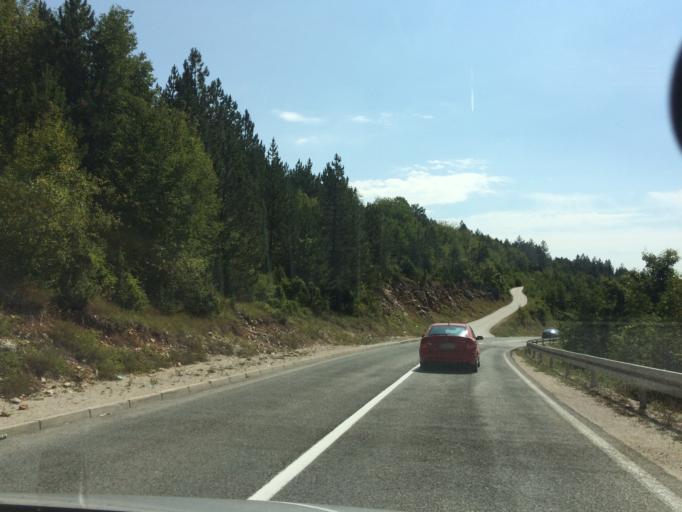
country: RS
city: Zlatibor
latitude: 43.6123
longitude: 19.7244
